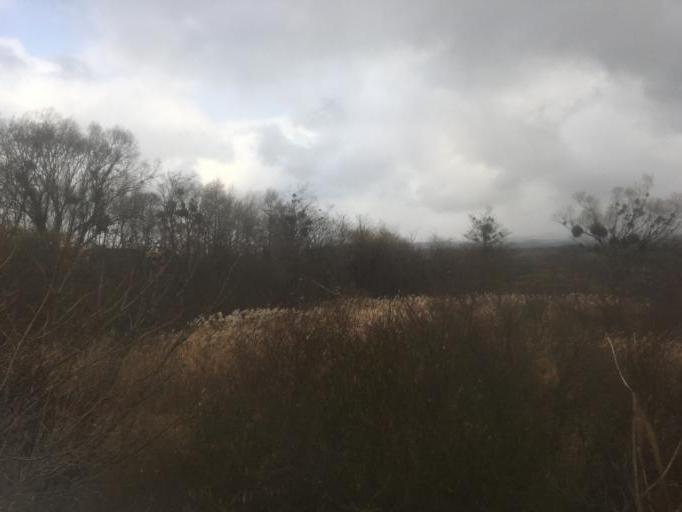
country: JP
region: Aomori
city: Goshogawara
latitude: 41.1809
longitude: 140.4893
